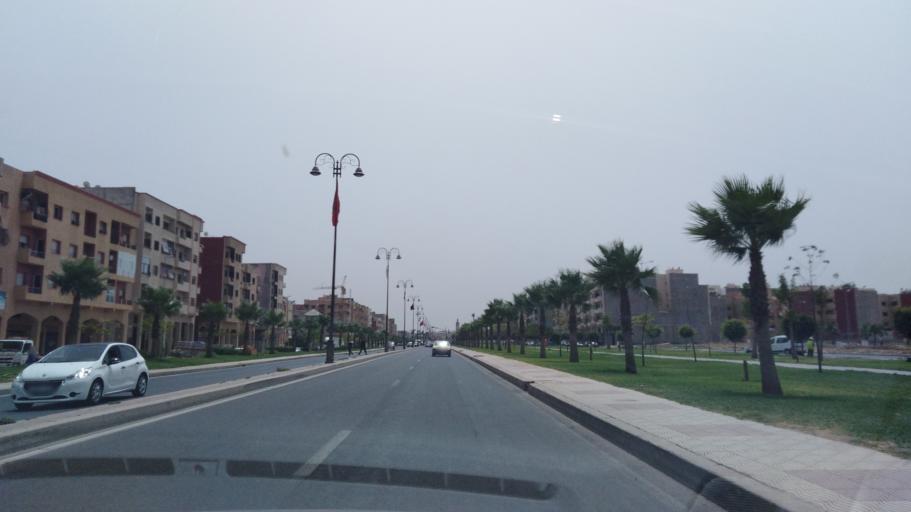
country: MA
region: Chaouia-Ouardigha
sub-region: Settat Province
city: Berrechid
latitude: 33.2779
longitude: -7.5816
